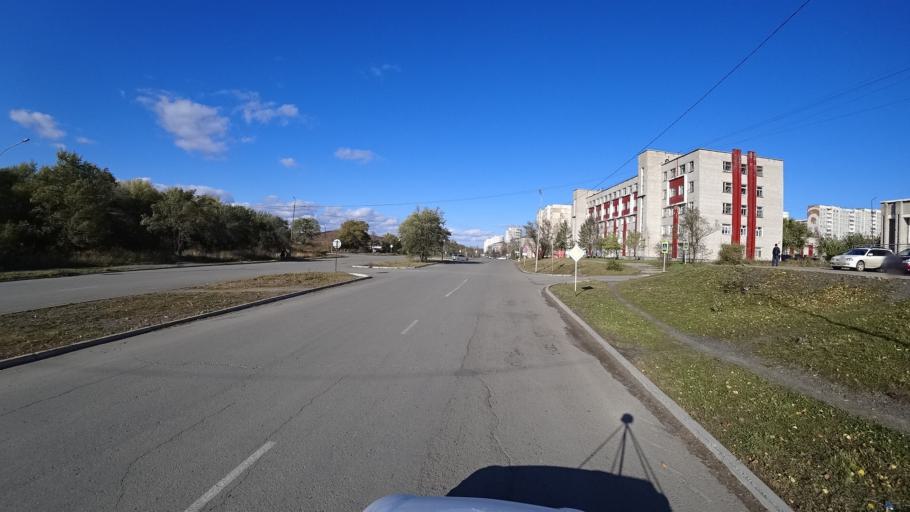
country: RU
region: Khabarovsk Krai
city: Amursk
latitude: 50.2422
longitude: 136.9141
